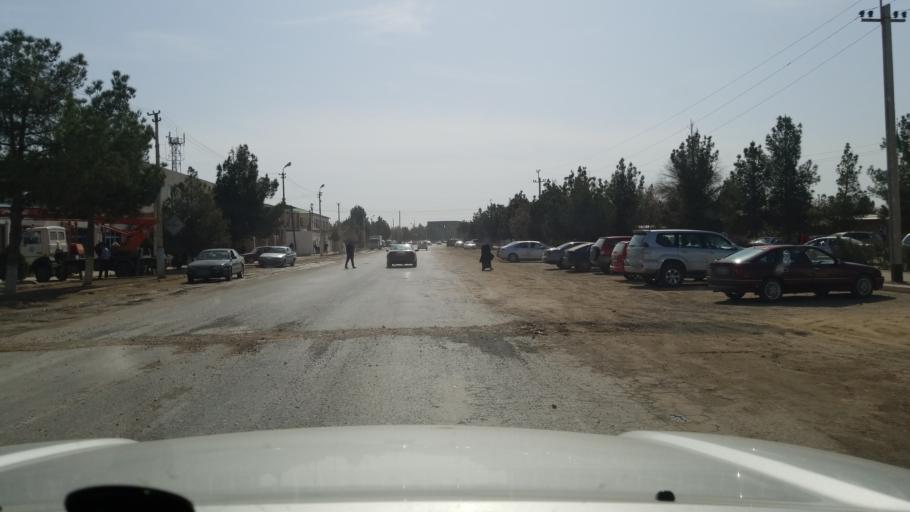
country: TM
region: Lebap
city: Sayat
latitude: 38.7808
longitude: 63.8792
